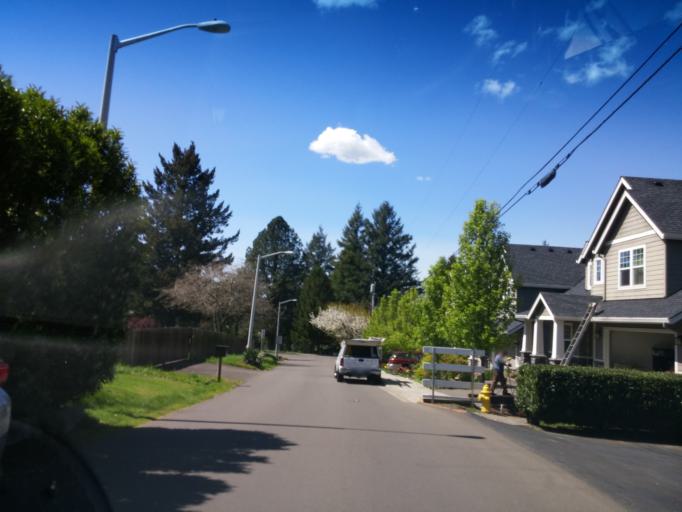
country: US
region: Oregon
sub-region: Washington County
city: West Haven
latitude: 45.5282
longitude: -122.7812
